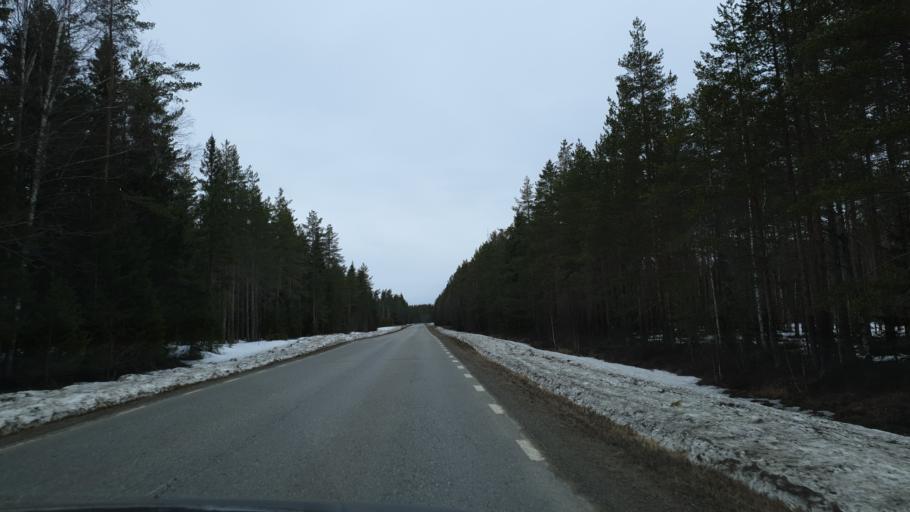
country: SE
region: Vaesterbotten
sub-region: Robertsfors Kommun
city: Robertsfors
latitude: 64.3976
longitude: 20.8871
